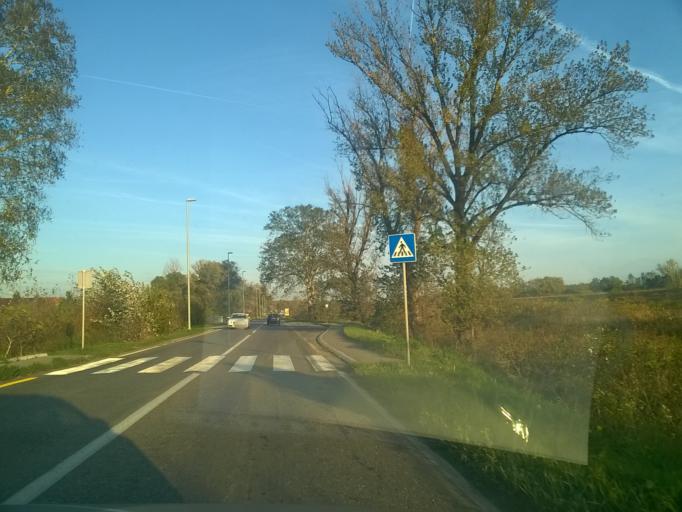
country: RS
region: Autonomna Pokrajina Vojvodina
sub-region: Juznobanatski Okrug
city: Pancevo
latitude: 44.8697
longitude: 20.6063
